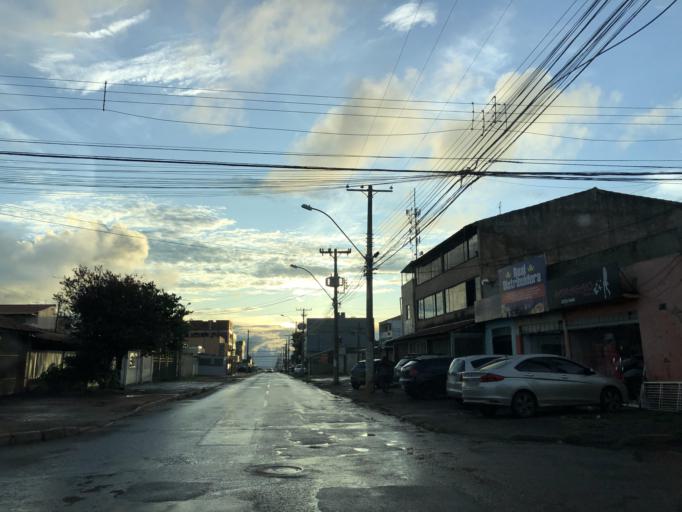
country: BR
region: Federal District
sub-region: Brasilia
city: Brasilia
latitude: -15.8285
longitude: -48.1011
